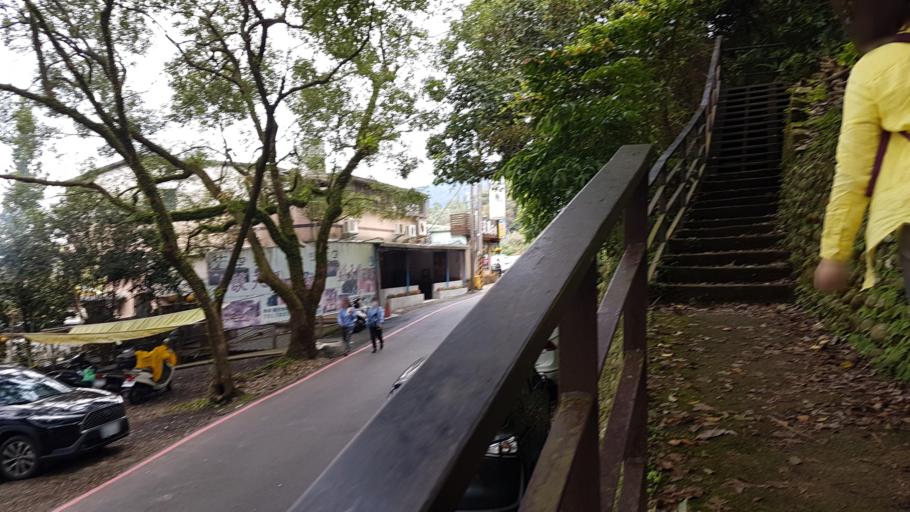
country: TW
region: Taipei
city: Taipei
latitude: 24.9685
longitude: 121.5849
